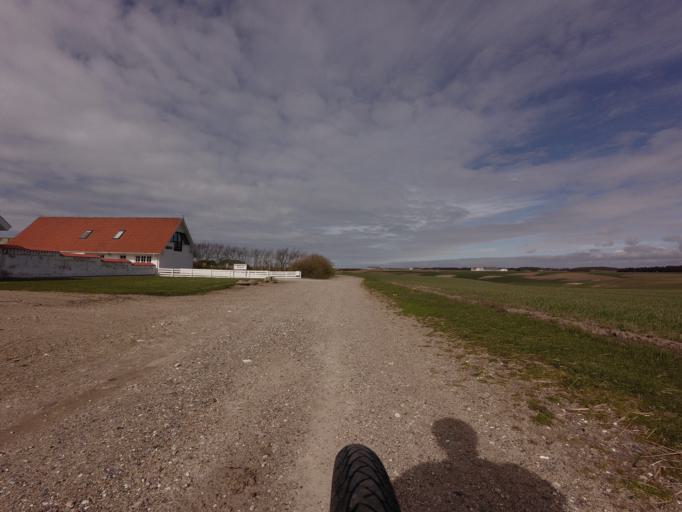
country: DK
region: North Denmark
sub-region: Jammerbugt Kommune
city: Pandrup
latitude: 57.3873
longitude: 9.7364
